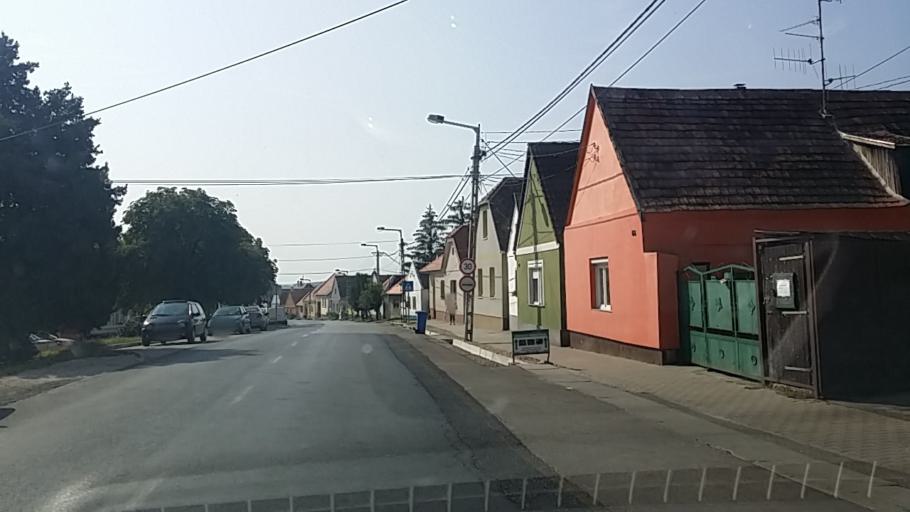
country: HU
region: Gyor-Moson-Sopron
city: Fertorakos
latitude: 47.7217
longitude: 16.6495
